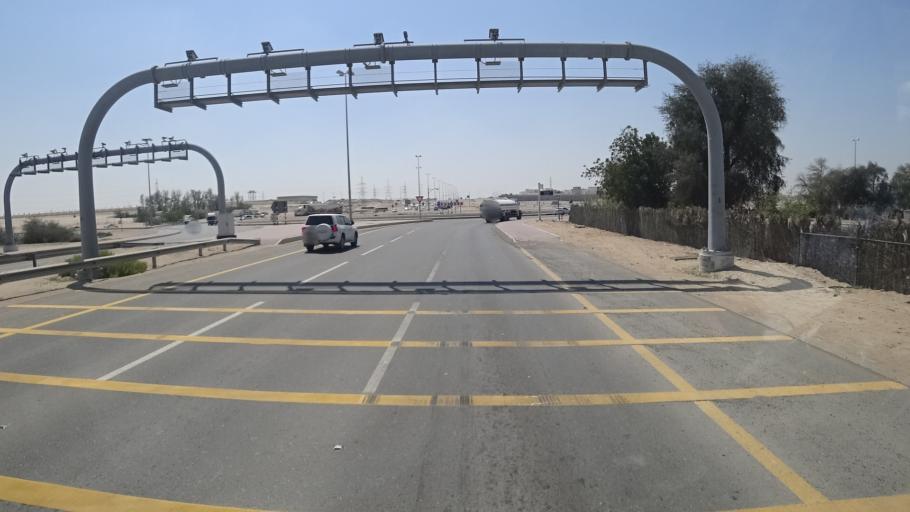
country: AE
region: Abu Dhabi
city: Abu Dhabi
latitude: 24.3042
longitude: 54.6688
